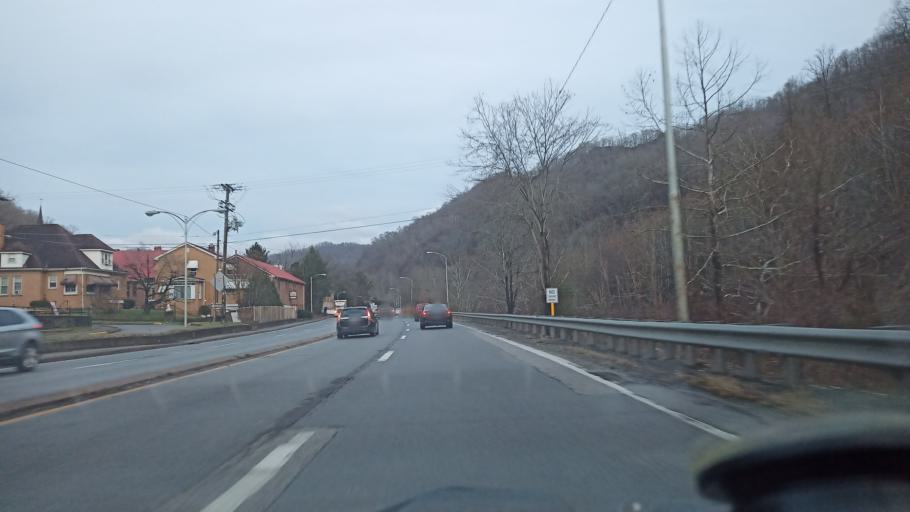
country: US
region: West Virginia
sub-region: Logan County
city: Logan
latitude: 37.8446
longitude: -81.9865
